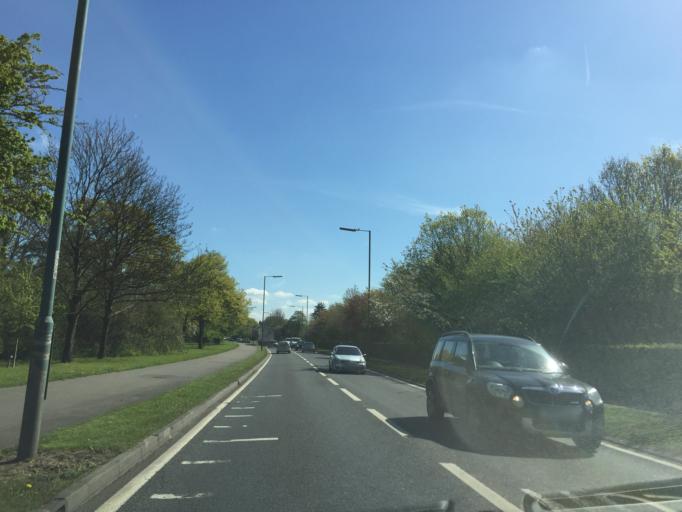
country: GB
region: England
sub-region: Essex
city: Harlow
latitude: 51.7544
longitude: 0.1083
